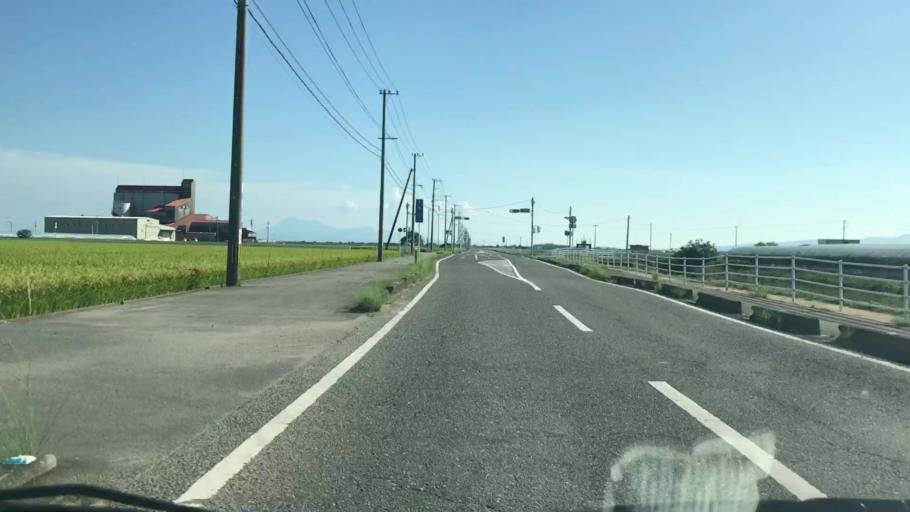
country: JP
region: Saga Prefecture
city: Okawa
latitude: 33.1761
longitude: 130.3119
